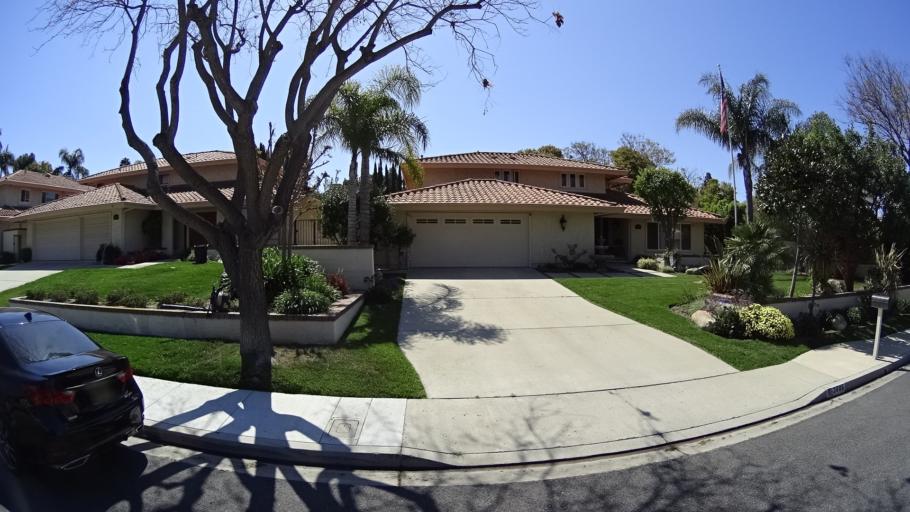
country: US
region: California
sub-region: Ventura County
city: Moorpark
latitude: 34.2319
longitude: -118.8521
